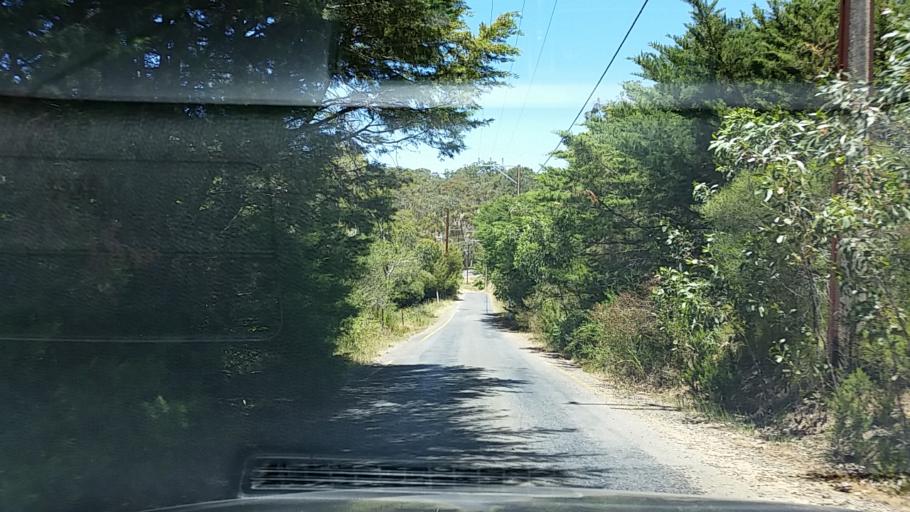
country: AU
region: South Australia
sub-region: Adelaide Hills
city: Crafers
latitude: -34.9873
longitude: 138.6923
